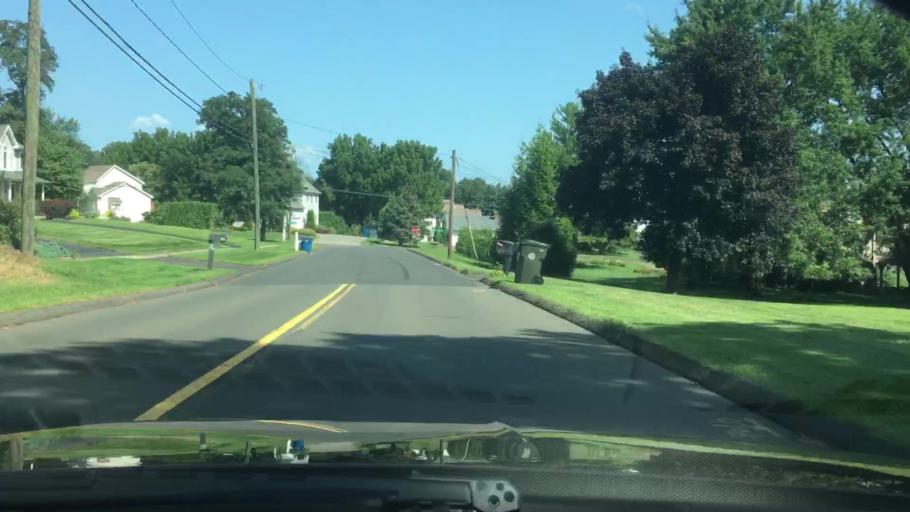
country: US
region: Connecticut
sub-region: Hartford County
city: Kensington
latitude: 41.6035
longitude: -72.7604
